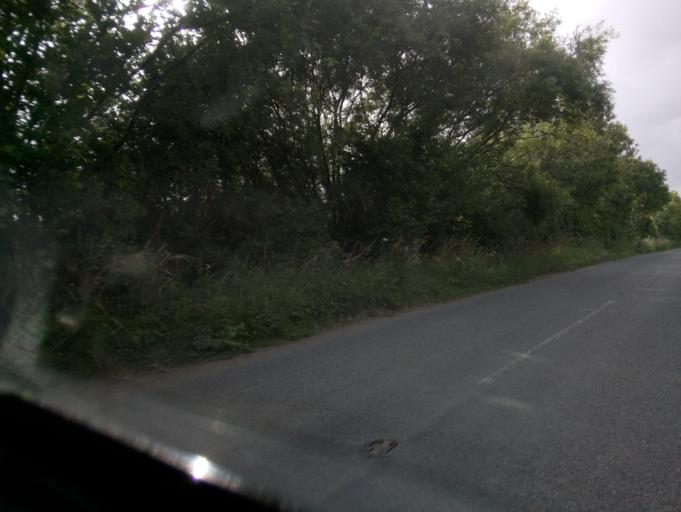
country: GB
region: England
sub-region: Gloucestershire
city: Chipping Campden
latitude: 52.0316
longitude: -1.7339
